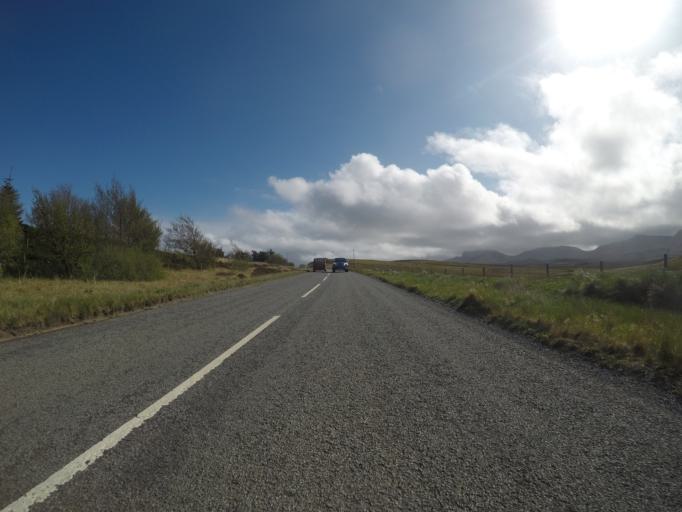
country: GB
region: Scotland
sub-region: Highland
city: Portree
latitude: 57.5788
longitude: -6.1574
